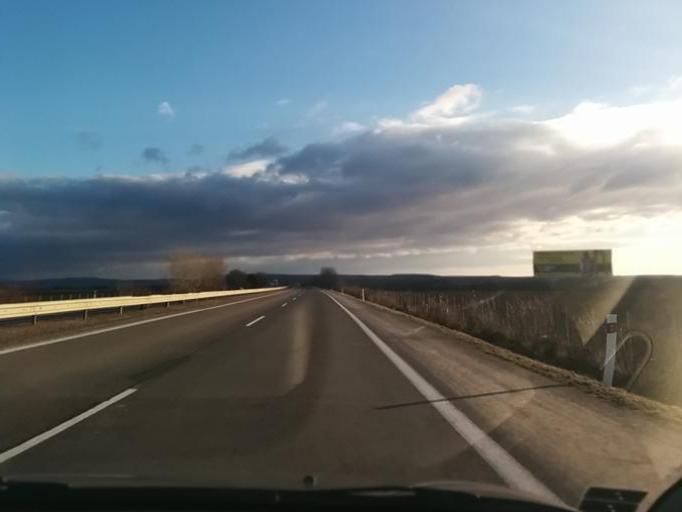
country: SK
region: Trnavsky
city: Leopoldov
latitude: 48.3690
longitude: 17.7150
